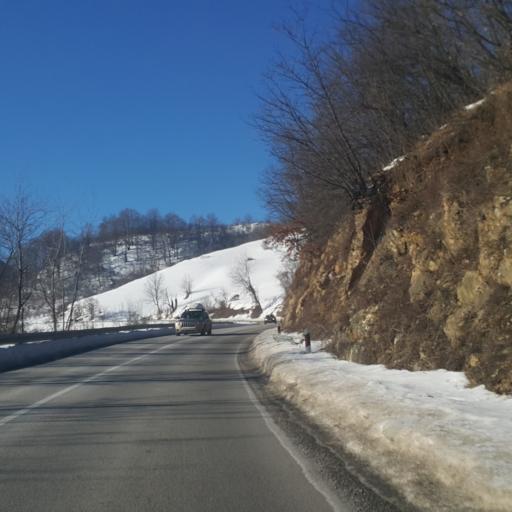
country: RS
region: Central Serbia
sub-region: Rasinski Okrug
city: Aleksandrovac
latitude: 43.3099
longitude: 20.9095
